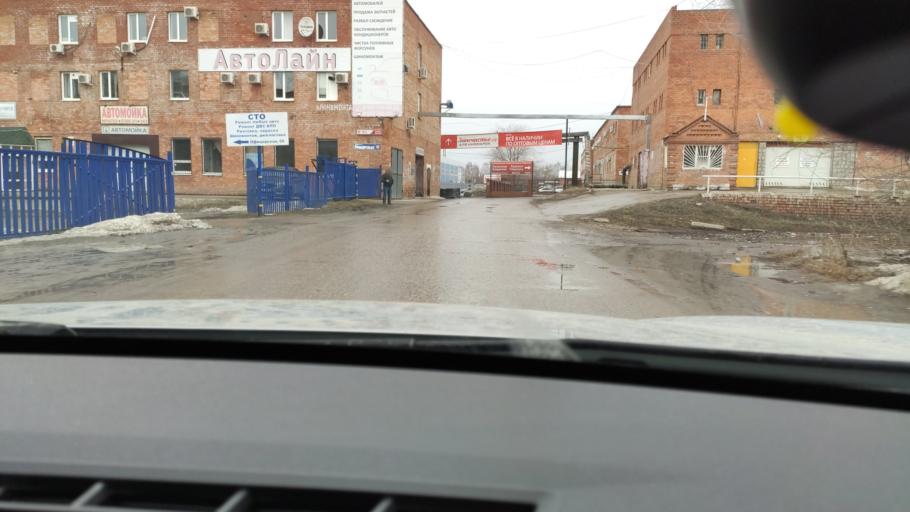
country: RU
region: Samara
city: Tol'yatti
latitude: 53.5397
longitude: 49.2711
